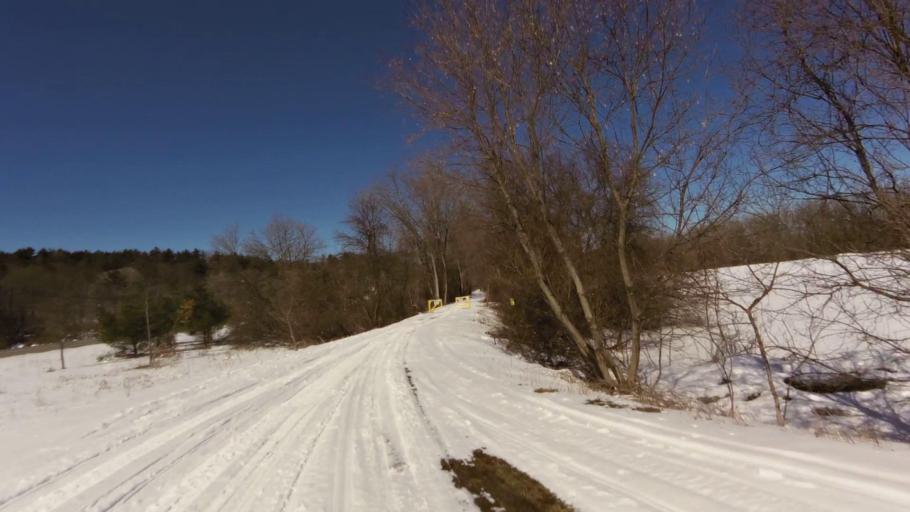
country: US
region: New York
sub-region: Allegany County
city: Houghton
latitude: 42.3731
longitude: -78.1430
